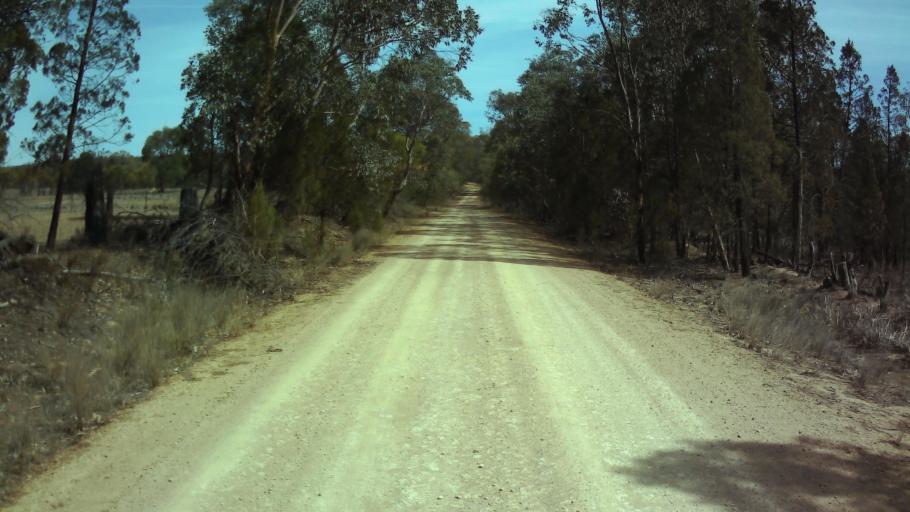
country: AU
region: New South Wales
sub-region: Weddin
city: Grenfell
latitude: -33.8730
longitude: 148.1480
